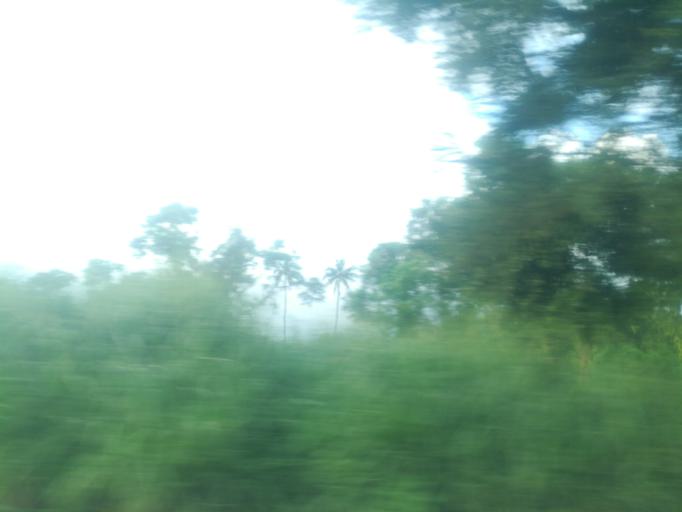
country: NG
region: Oyo
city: Ibadan
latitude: 7.3814
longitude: 3.8394
